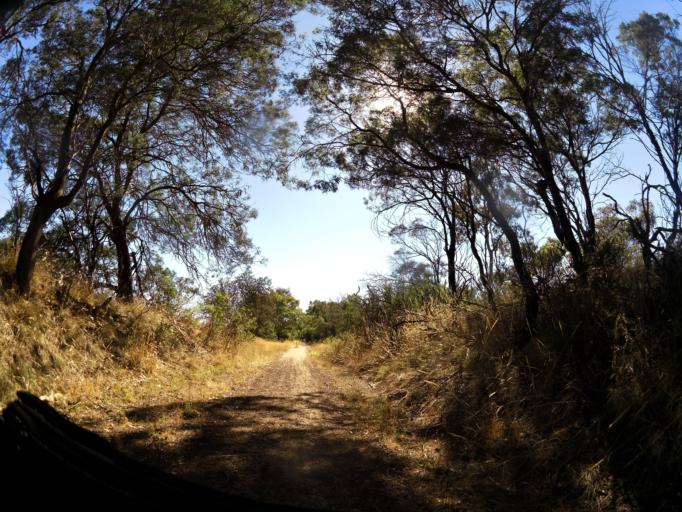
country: AU
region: Victoria
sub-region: Ballarat North
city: Delacombe
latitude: -37.6697
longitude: 143.4567
